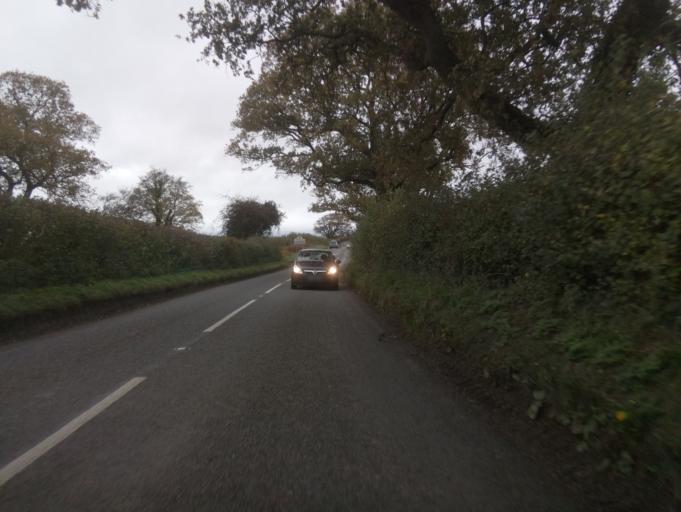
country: GB
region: England
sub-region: Dorset
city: Sherborne
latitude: 50.9775
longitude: -2.5619
